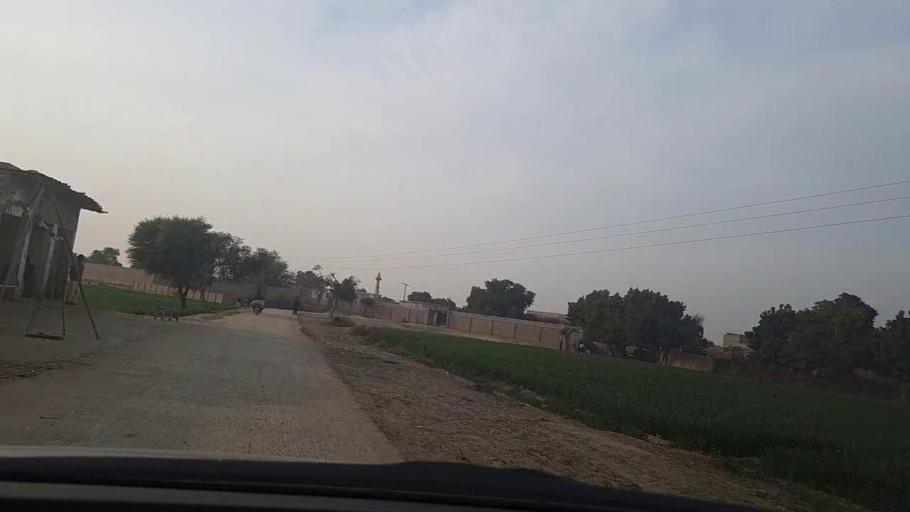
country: PK
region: Sindh
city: Daulatpur
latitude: 26.3371
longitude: 68.0208
